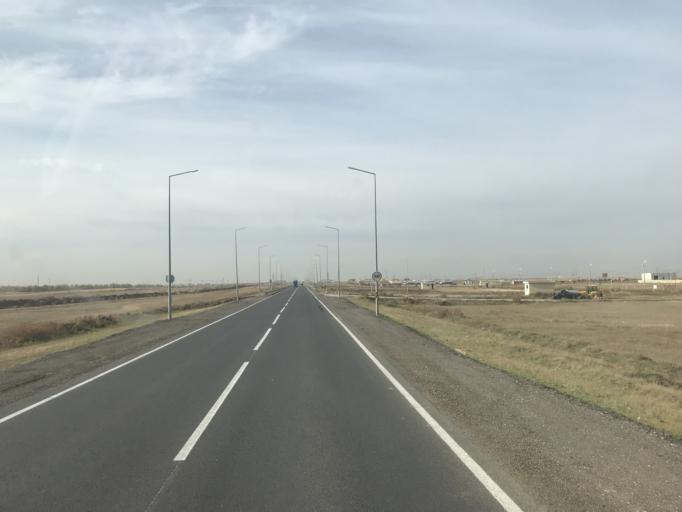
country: KZ
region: Astana Qalasy
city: Astana
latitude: 51.2605
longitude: 71.4020
